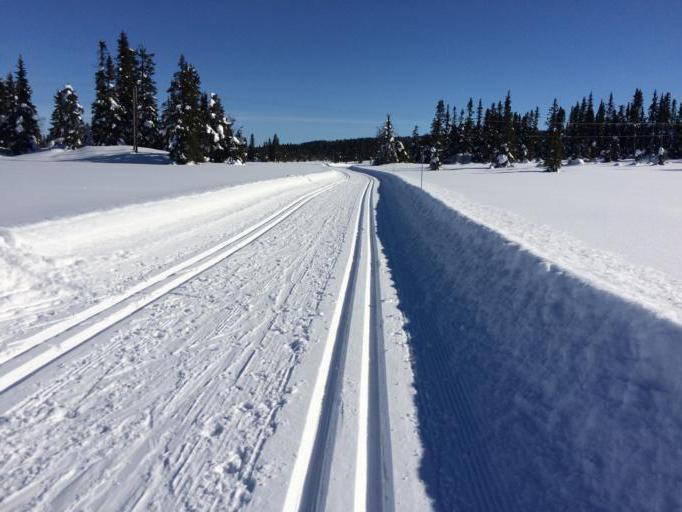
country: NO
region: Oppland
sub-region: Gausdal
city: Segalstad bru
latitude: 61.3272
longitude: 10.0820
